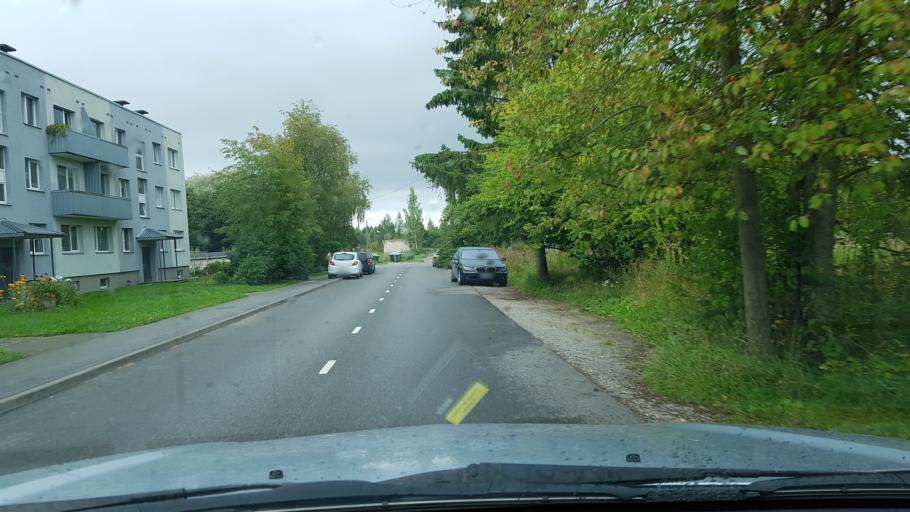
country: EE
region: Harju
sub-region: Joelaehtme vald
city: Loo
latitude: 59.4027
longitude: 24.9308
